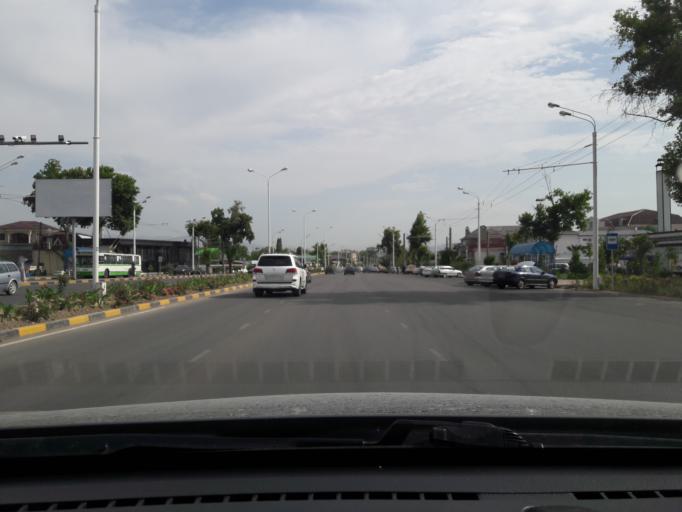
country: TJ
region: Dushanbe
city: Dushanbe
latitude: 38.5405
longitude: 68.7551
